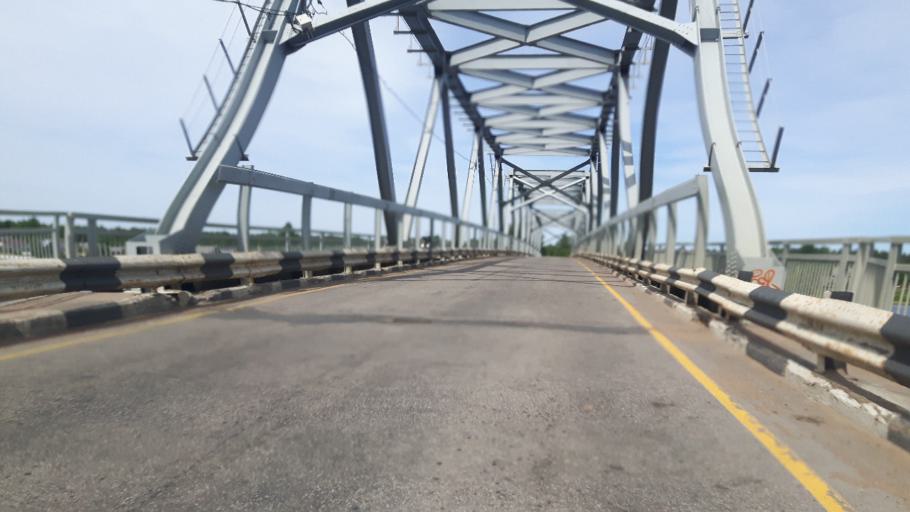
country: RU
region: Leningrad
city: Ust'-Luga
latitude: 59.6524
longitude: 28.2587
